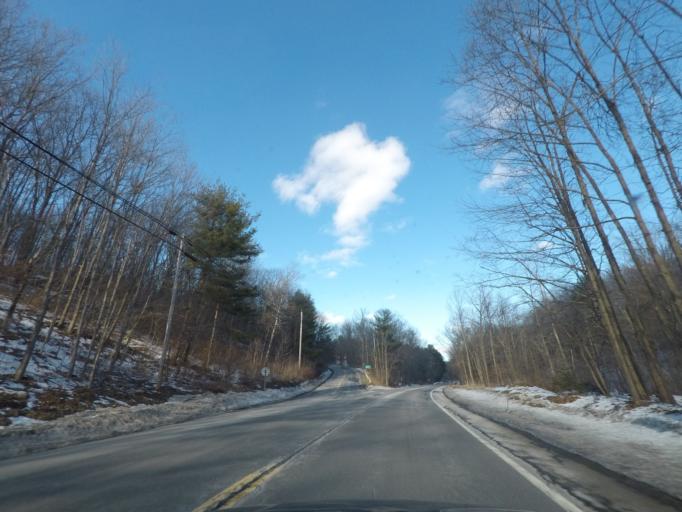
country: US
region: Massachusetts
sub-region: Berkshire County
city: West Stockbridge
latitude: 42.3156
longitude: -73.4722
